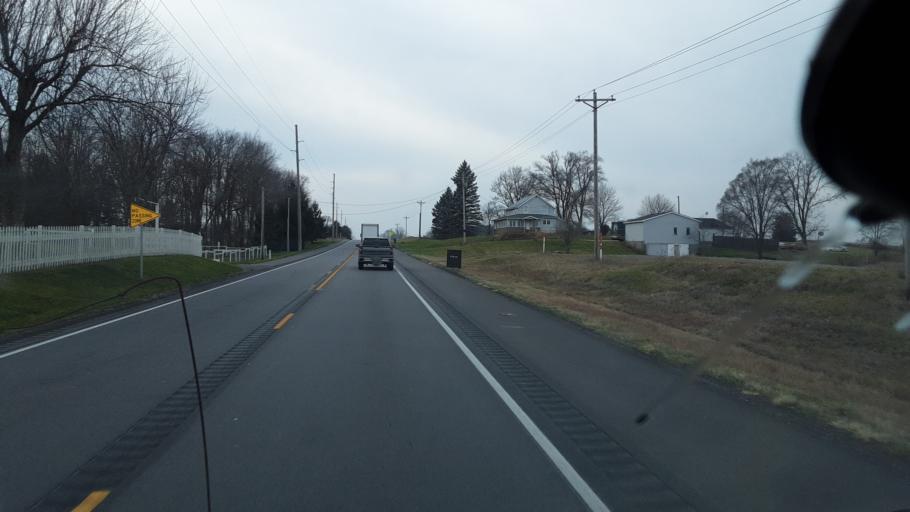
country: US
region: Indiana
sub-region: LaGrange County
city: Lagrange
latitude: 41.6419
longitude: -85.2166
